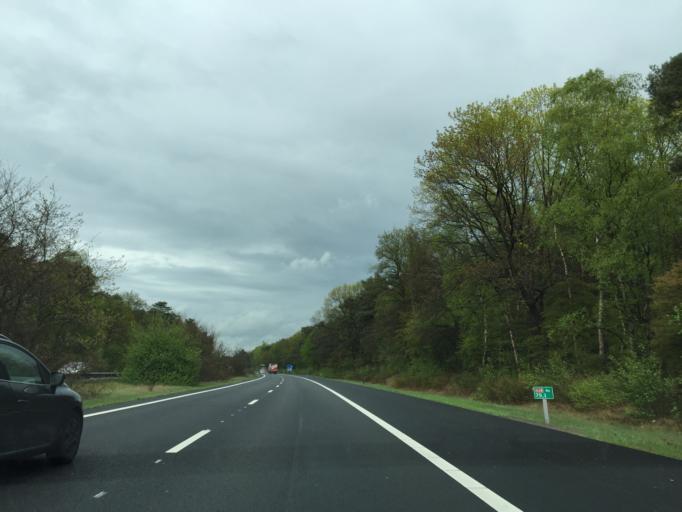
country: NL
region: Gelderland
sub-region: Gemeente Oldebroek
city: Oldebroek
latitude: 52.4447
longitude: 5.9722
